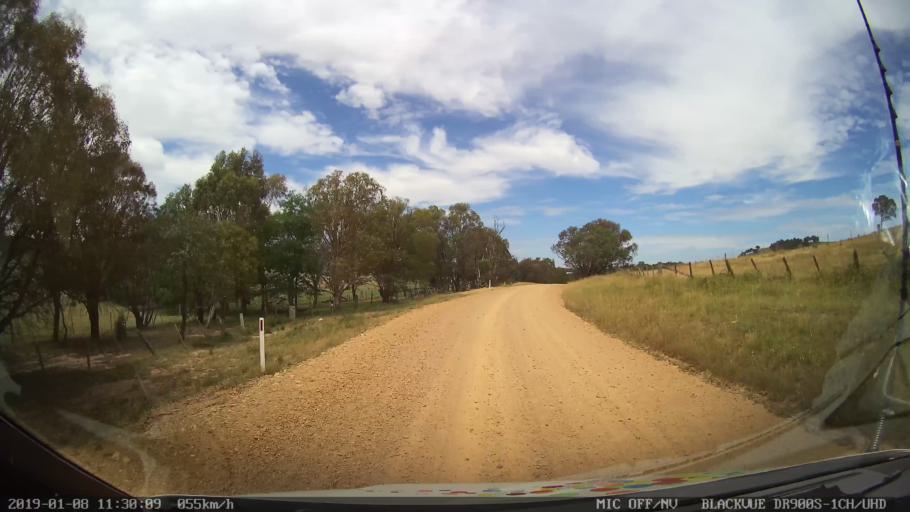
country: AU
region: New South Wales
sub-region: Guyra
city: Guyra
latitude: -30.3059
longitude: 151.5457
